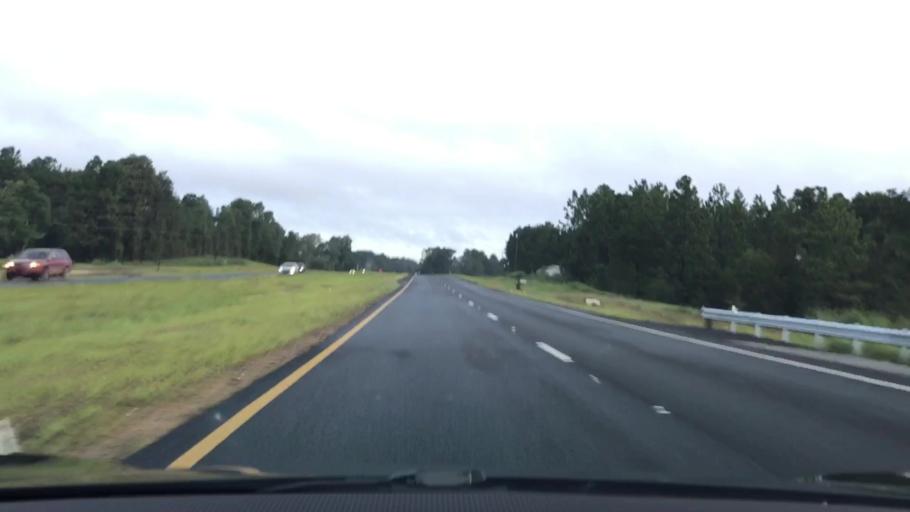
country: US
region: Florida
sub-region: Walton County
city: DeFuniak Springs
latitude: 30.6541
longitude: -86.1156
